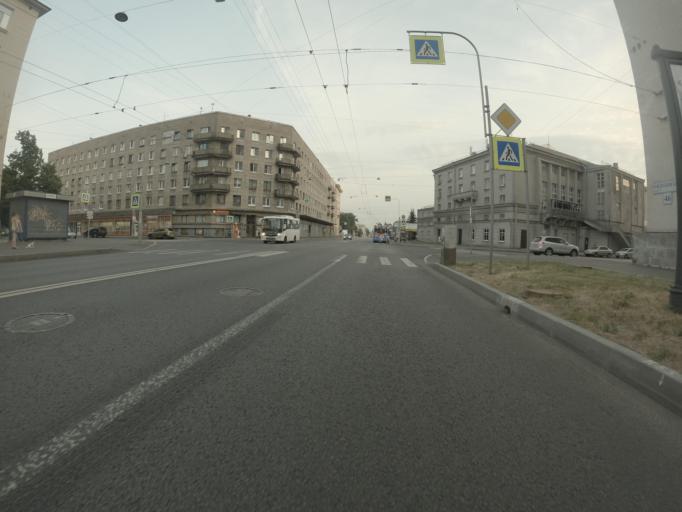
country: RU
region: Leningrad
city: Finlyandskiy
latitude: 59.9717
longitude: 30.3875
